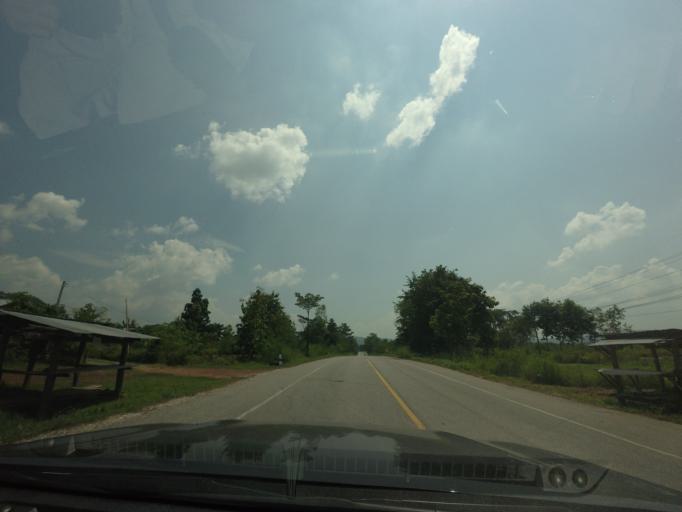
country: TH
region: Uttaradit
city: Thong Saen Khan
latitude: 17.3201
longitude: 100.3887
